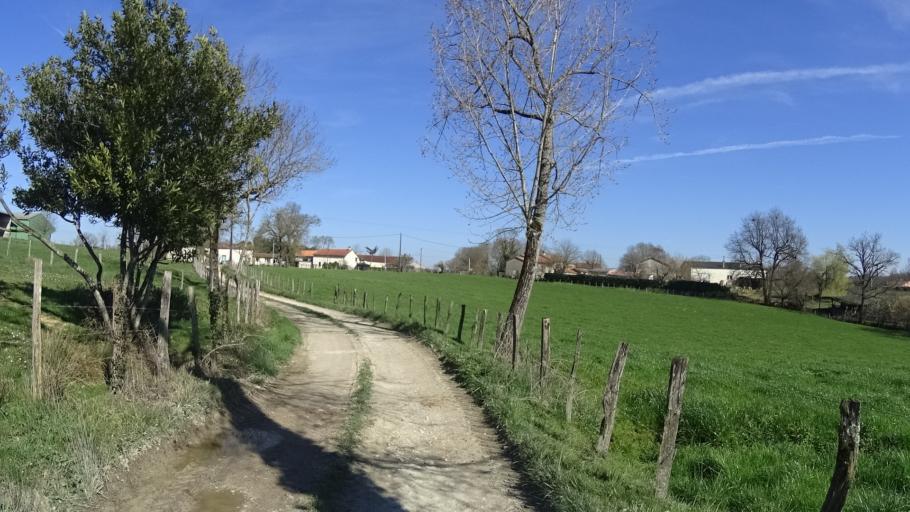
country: FR
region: Aquitaine
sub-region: Departement de la Dordogne
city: Riberac
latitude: 45.2162
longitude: 0.3287
